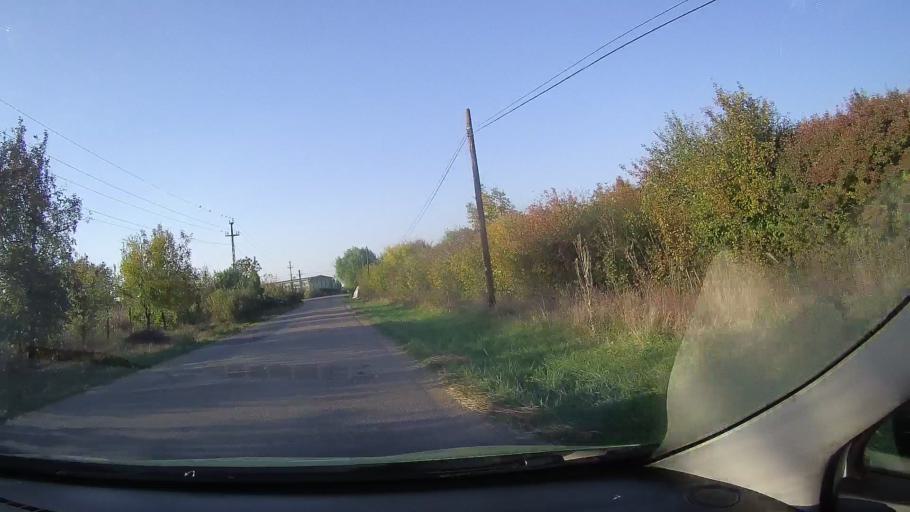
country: RO
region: Bihor
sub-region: Comuna Bors
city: Bors
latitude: 47.1137
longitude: 21.8230
